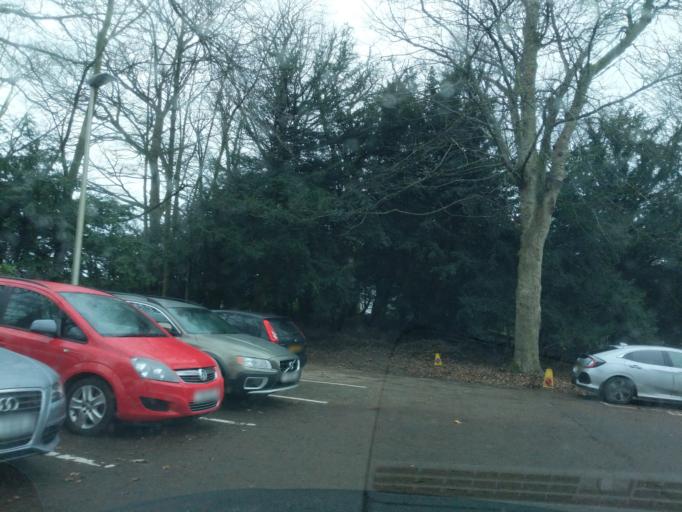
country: GB
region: Scotland
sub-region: Midlothian
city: Loanhead
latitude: 55.9020
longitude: -3.1692
